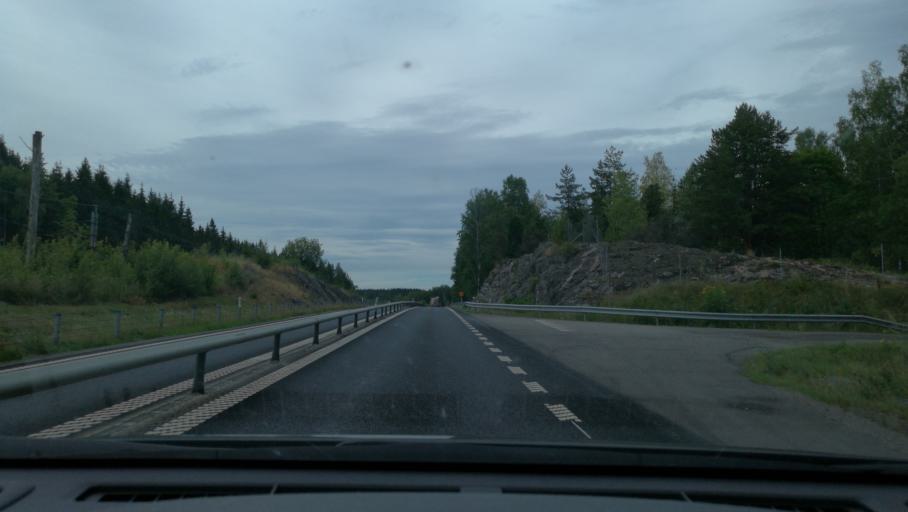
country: SE
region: Soedermanland
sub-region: Katrineholms Kommun
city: Katrineholm
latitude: 58.8718
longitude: 16.1970
